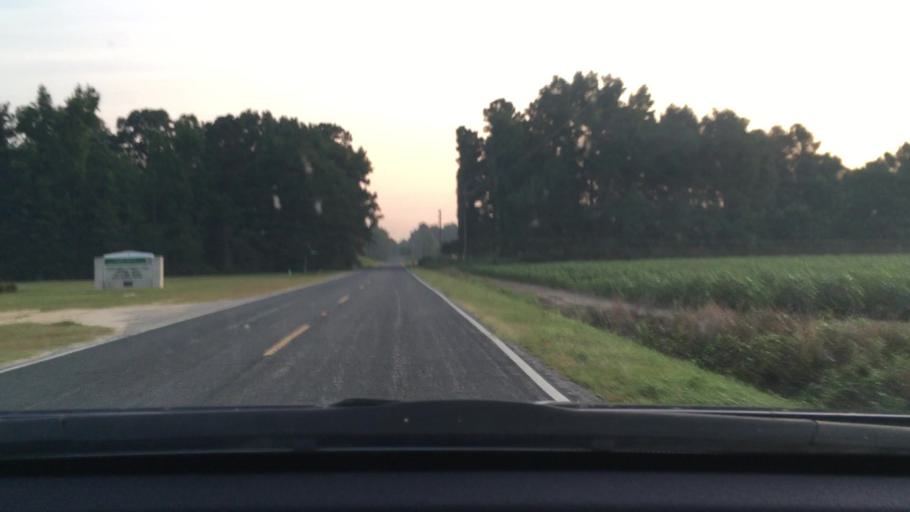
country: US
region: South Carolina
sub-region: Lee County
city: Bishopville
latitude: 34.1865
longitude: -80.1423
